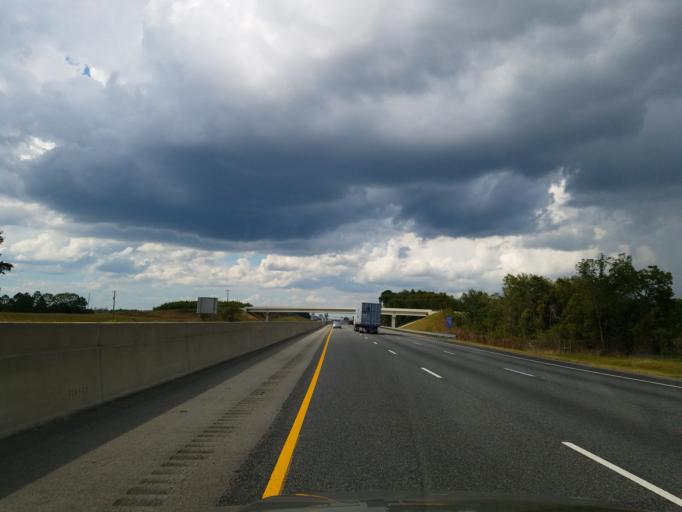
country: US
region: Georgia
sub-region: Turner County
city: Ashburn
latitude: 31.6701
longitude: -83.6112
